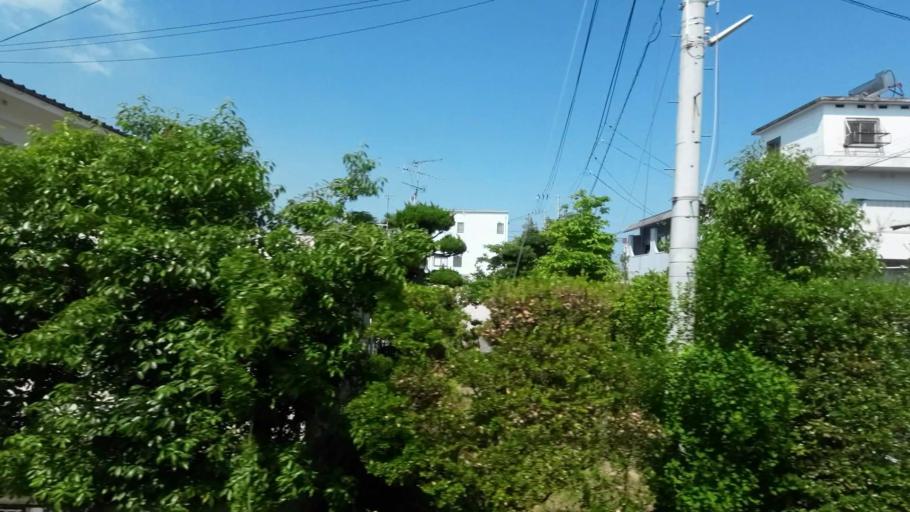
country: JP
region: Ehime
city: Kawanoecho
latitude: 34.0101
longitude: 133.5754
